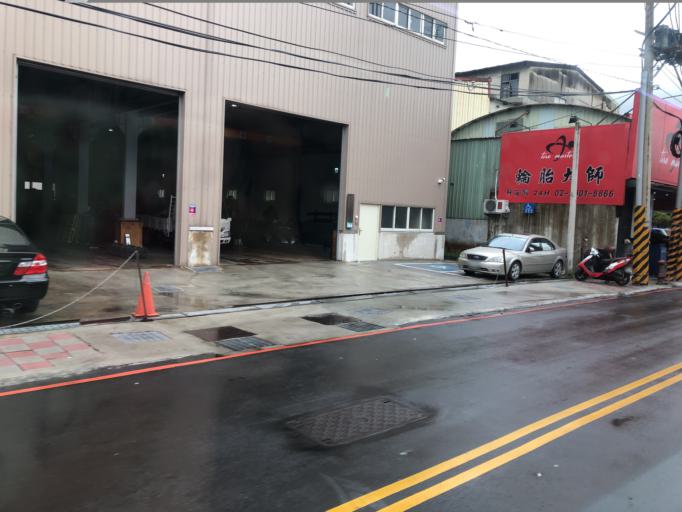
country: TW
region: Taipei
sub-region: Taipei
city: Banqiao
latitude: 25.0294
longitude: 121.4260
